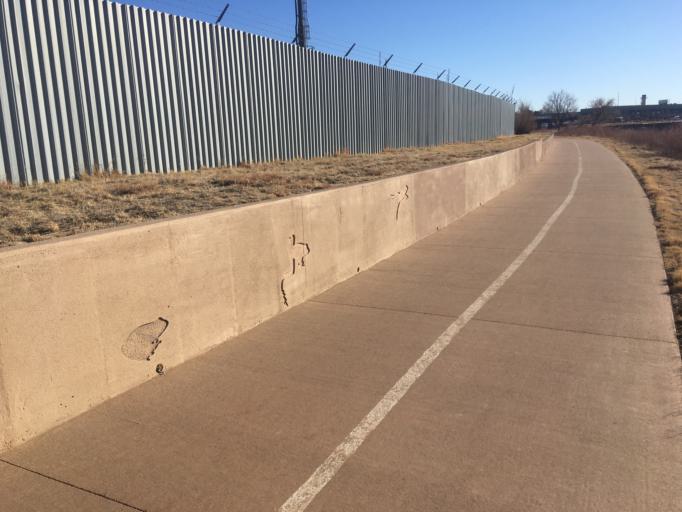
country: US
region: Colorado
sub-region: Adams County
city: Commerce City
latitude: 39.8027
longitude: -104.9399
